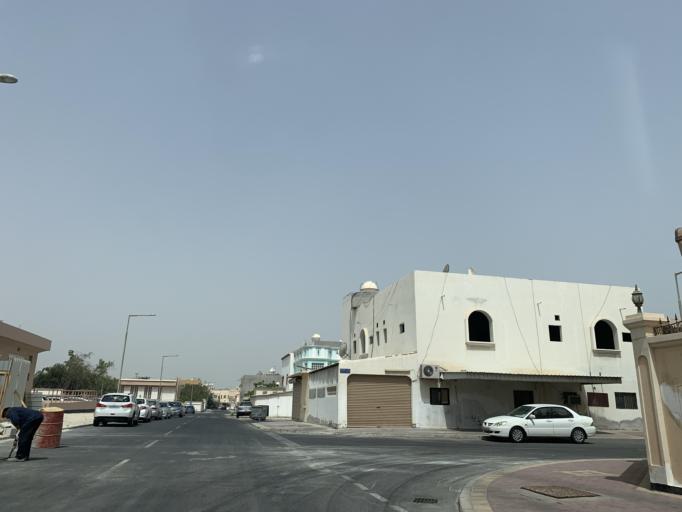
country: BH
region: Northern
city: Madinat `Isa
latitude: 26.1644
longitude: 50.5614
